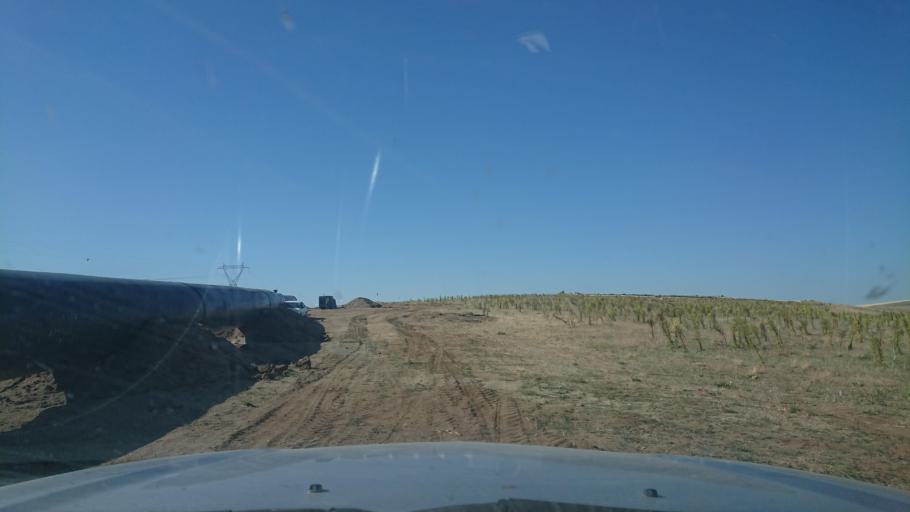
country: TR
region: Aksaray
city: Agacoren
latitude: 38.8432
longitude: 33.9439
